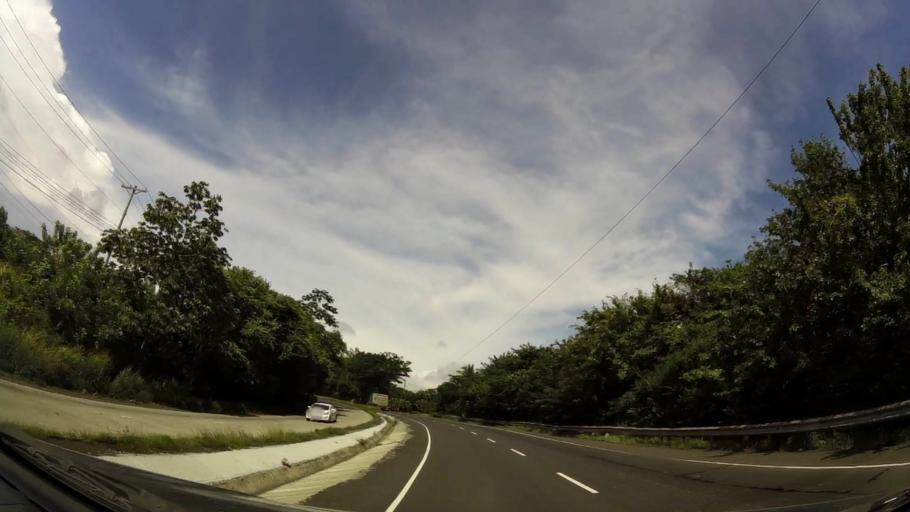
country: PA
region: Panama
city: Capira
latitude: 8.6754
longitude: -79.8688
